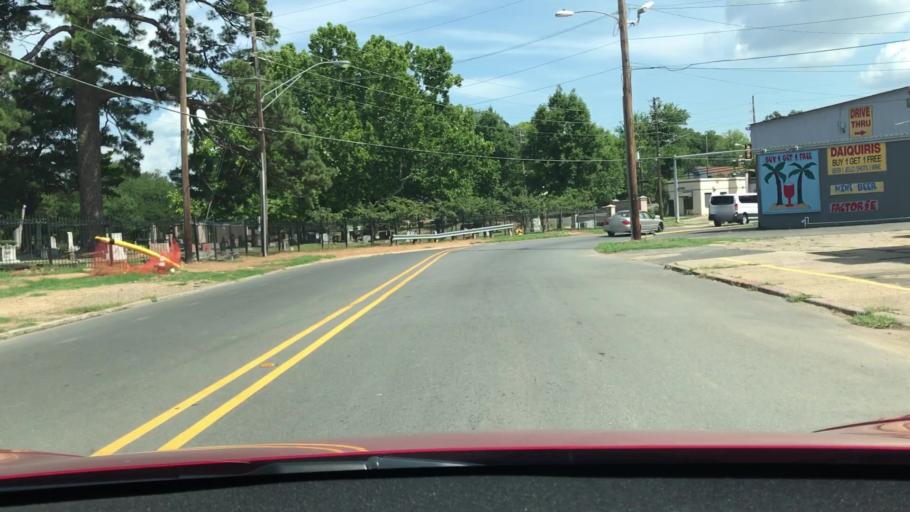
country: US
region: Louisiana
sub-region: Bossier Parish
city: Bossier City
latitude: 32.5007
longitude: -93.7335
